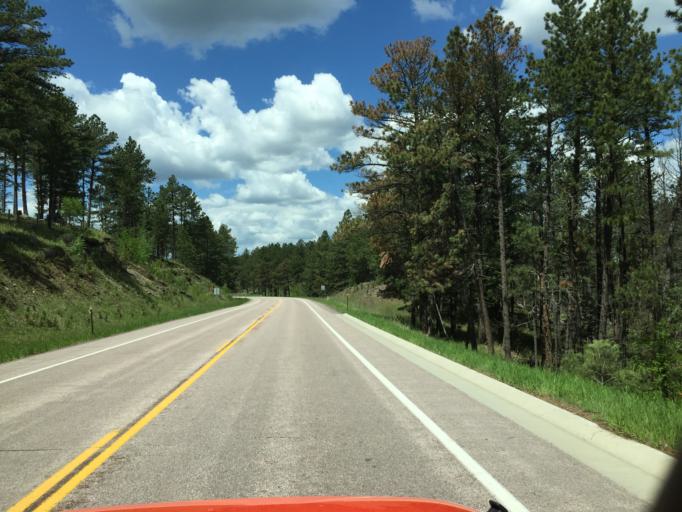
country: US
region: South Dakota
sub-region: Custer County
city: Custer
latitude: 43.8987
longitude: -103.4939
